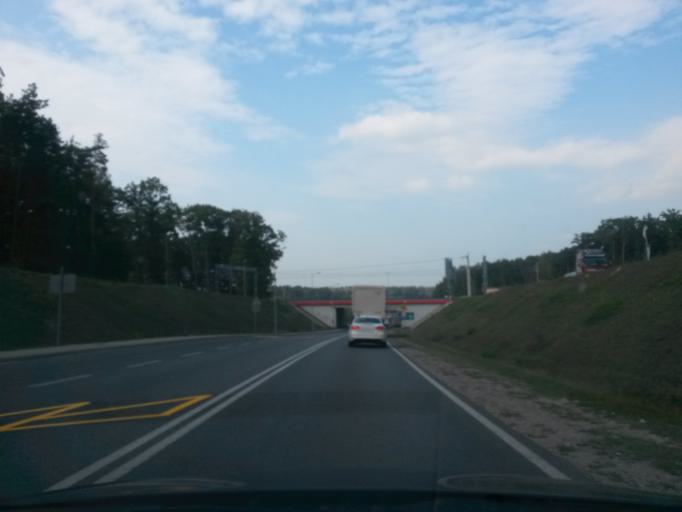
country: PL
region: Lesser Poland Voivodeship
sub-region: Powiat brzeski
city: Brzesko
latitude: 49.9861
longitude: 20.5927
